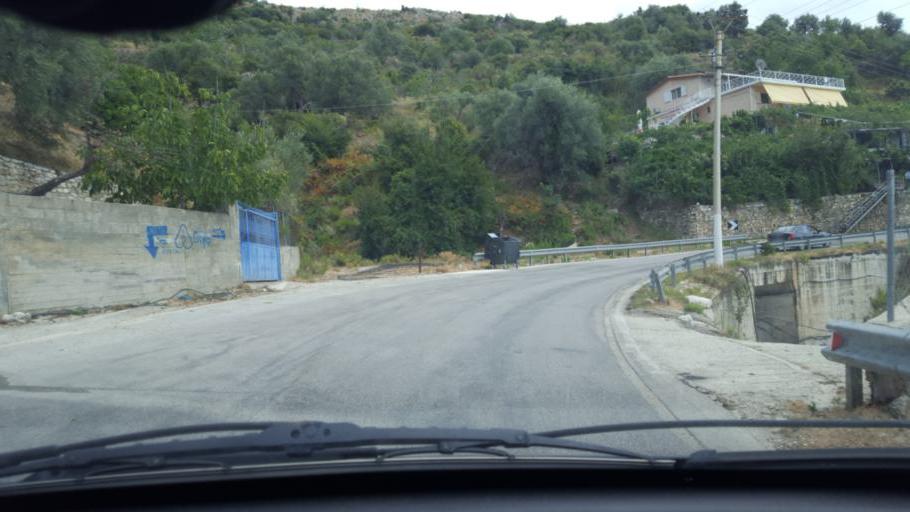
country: AL
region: Vlore
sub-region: Rrethi i Sarandes
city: Lukove
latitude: 40.0536
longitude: 19.8700
